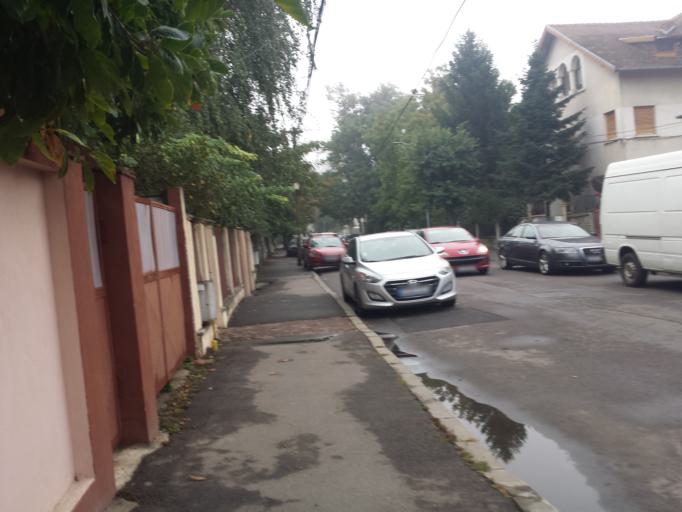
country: RO
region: Ilfov
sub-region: Comuna Chiajna
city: Rosu
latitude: 44.4702
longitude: 26.0605
